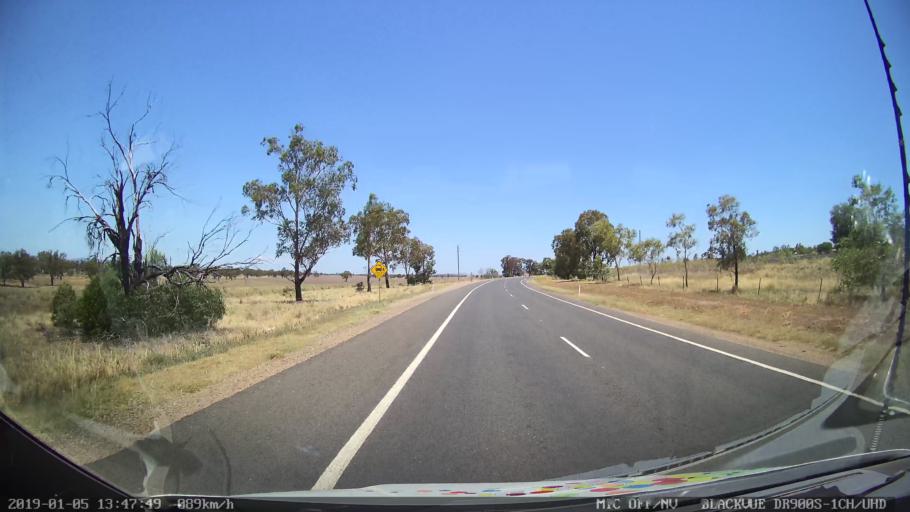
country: AU
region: New South Wales
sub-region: Gunnedah
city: Gunnedah
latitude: -30.9929
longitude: 150.2792
